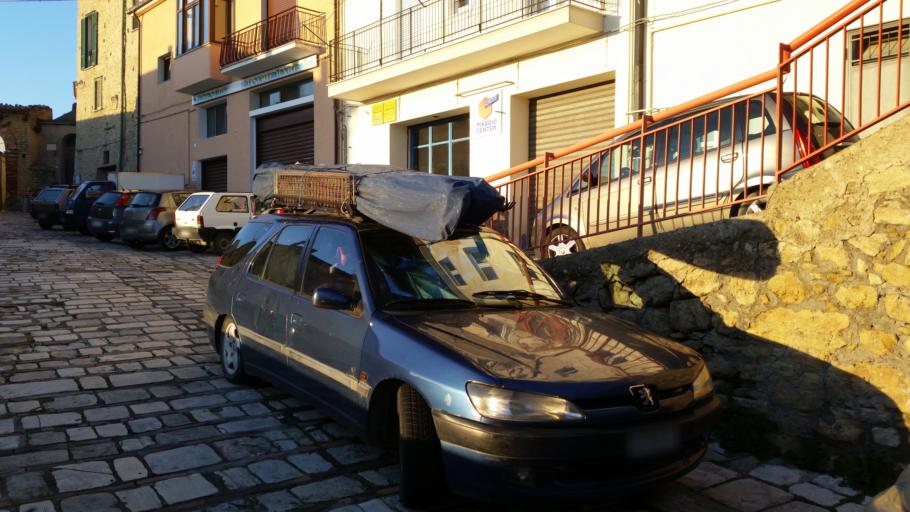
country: IT
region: Basilicate
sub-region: Provincia di Matera
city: Tricarico
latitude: 40.6201
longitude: 16.1469
